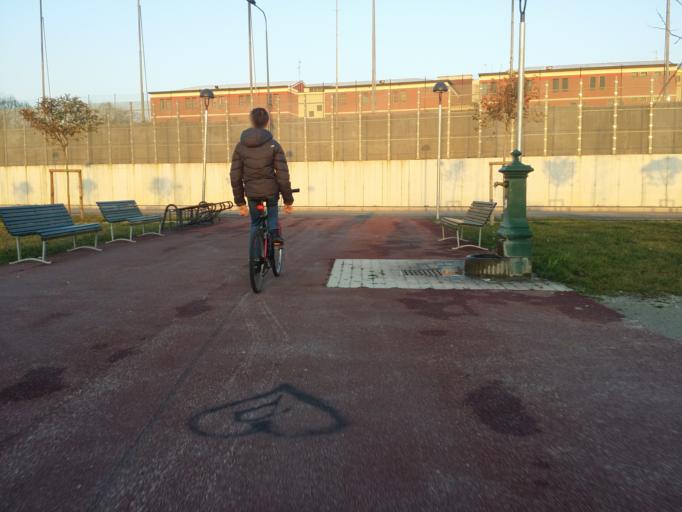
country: IT
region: Lombardy
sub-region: Citta metropolitana di Milano
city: Cesano Boscone
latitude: 45.4526
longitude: 9.1088
